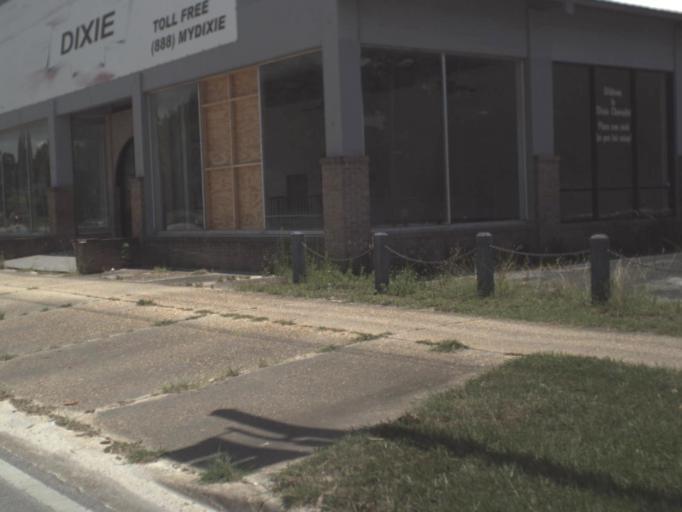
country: US
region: Florida
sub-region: Dixie County
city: Cross City
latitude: 29.6360
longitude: -83.1275
